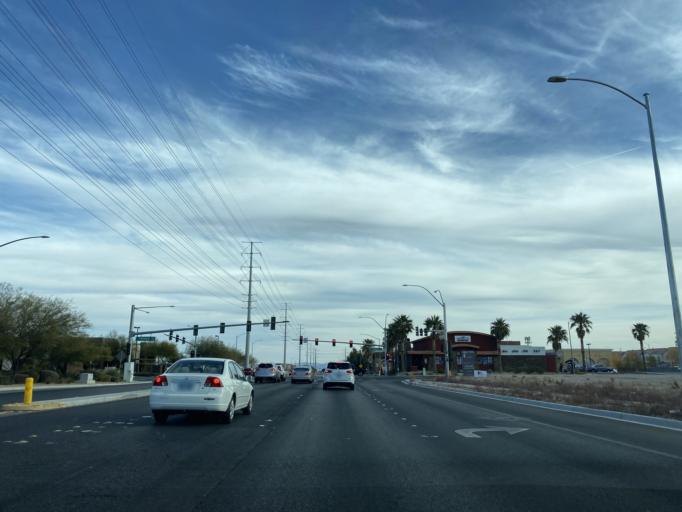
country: US
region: Nevada
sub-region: Clark County
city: Enterprise
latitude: 36.0556
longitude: -115.2530
